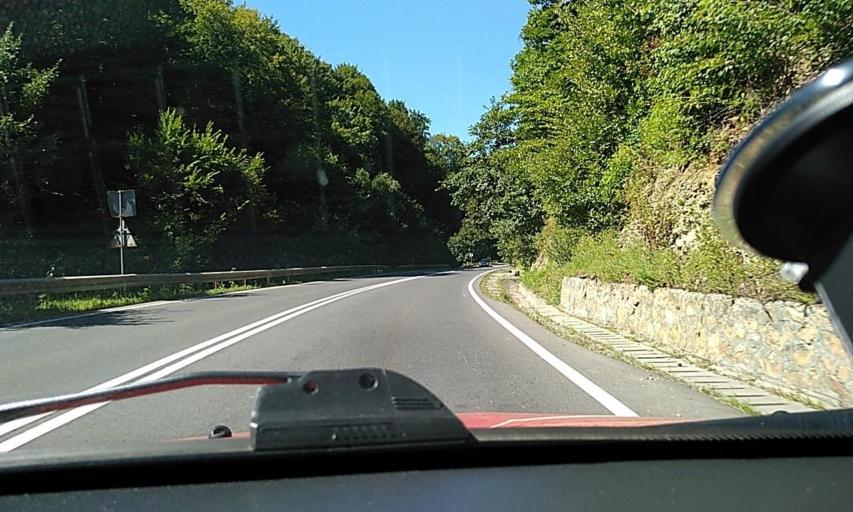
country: RO
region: Brasov
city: Maierus
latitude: 45.8974
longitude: 25.4498
